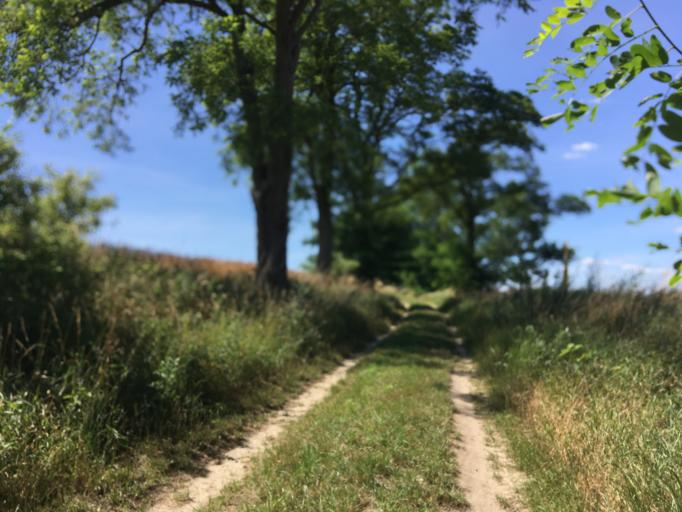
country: DE
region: Brandenburg
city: Brussow
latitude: 53.3278
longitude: 14.0779
